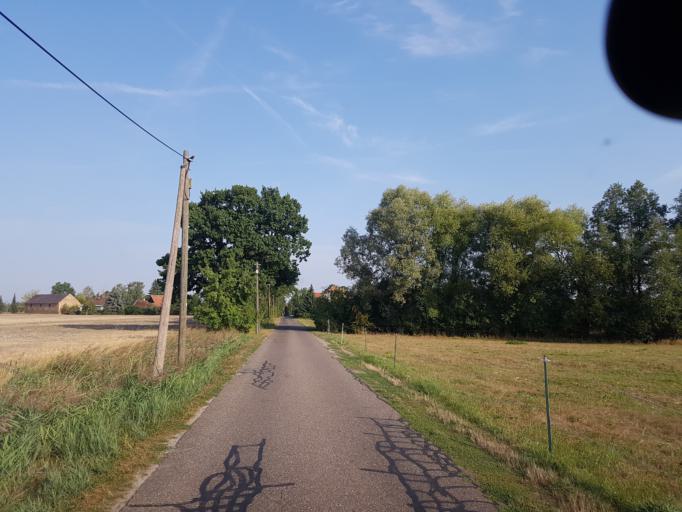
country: DE
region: Brandenburg
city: Finsterwalde
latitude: 51.6611
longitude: 13.7161
